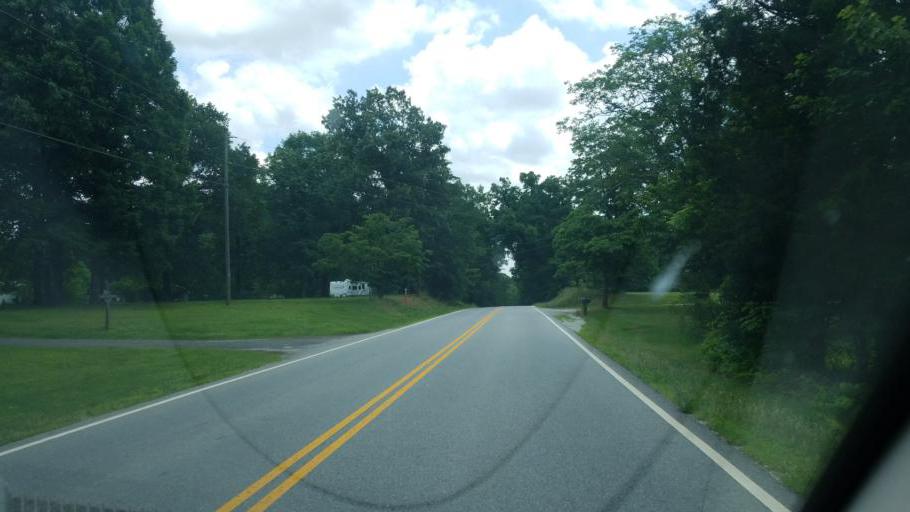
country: US
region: Virginia
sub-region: Appomattox County
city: Appomattox
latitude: 37.5495
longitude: -78.8346
